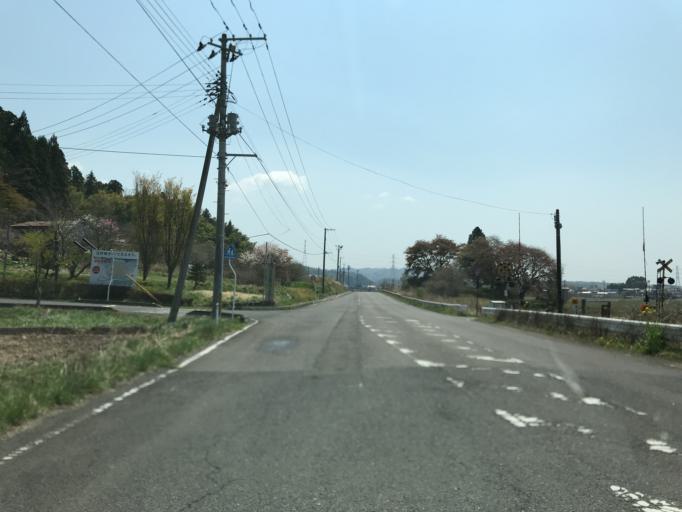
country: JP
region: Fukushima
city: Ishikawa
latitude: 37.0916
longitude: 140.4118
